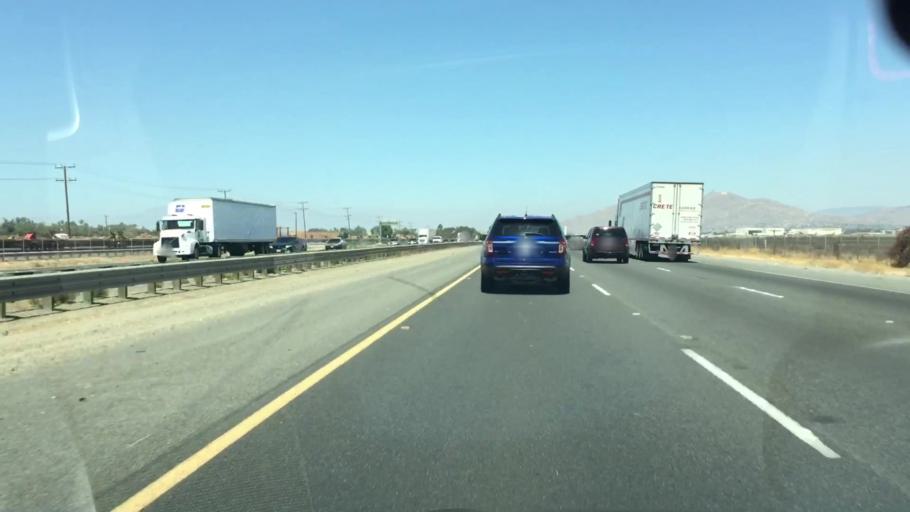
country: US
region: California
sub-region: Riverside County
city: March Air Force Base
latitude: 33.8715
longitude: -117.2635
